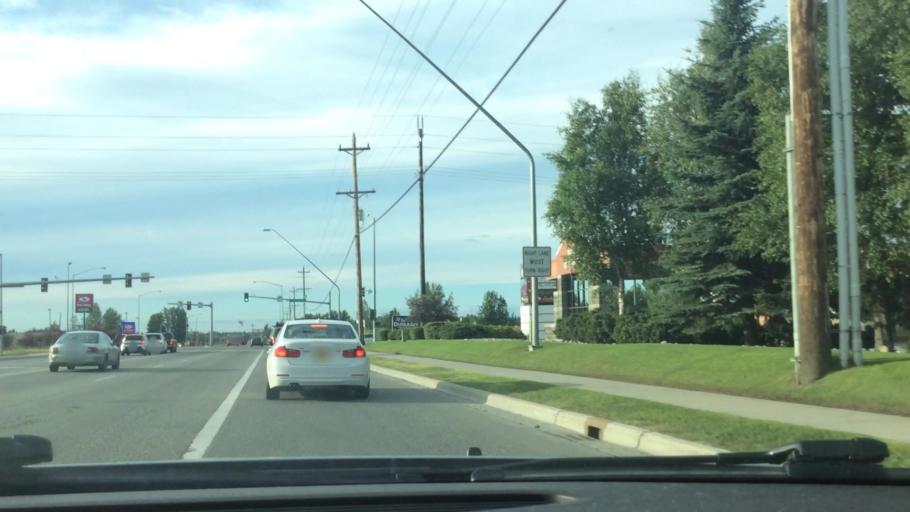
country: US
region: Alaska
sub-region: Anchorage Municipality
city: Anchorage
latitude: 61.1220
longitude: -149.8635
